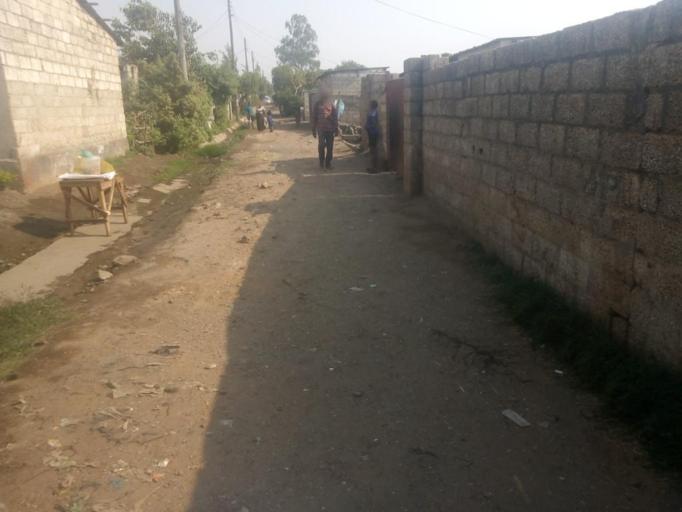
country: ZM
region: Lusaka
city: Lusaka
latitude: -15.4044
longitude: 28.3613
